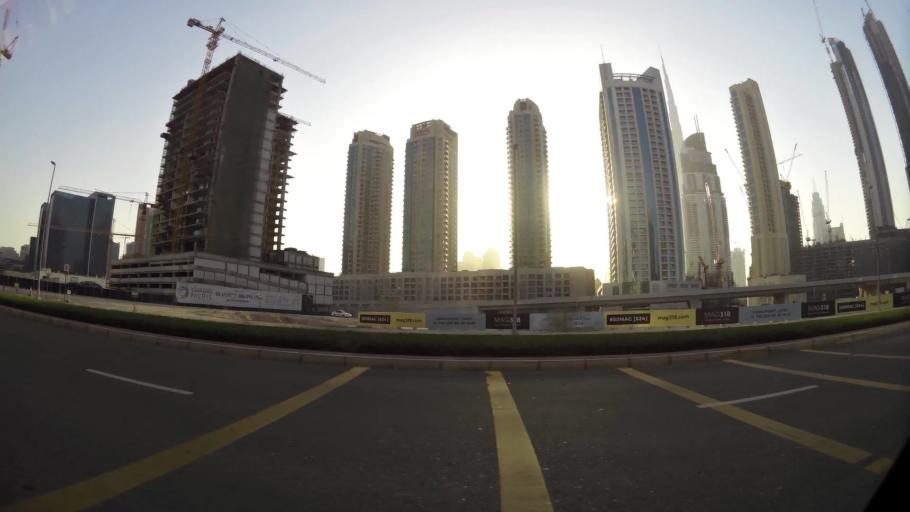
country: AE
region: Dubai
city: Dubai
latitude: 25.1902
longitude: 55.2841
